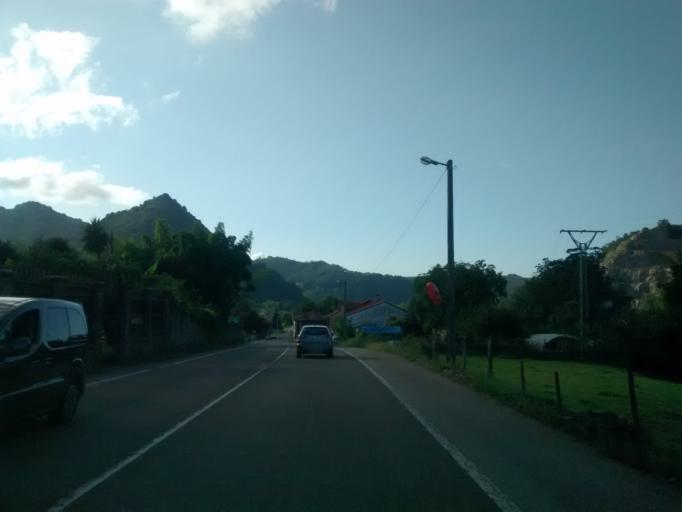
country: ES
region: Cantabria
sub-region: Provincia de Cantabria
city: Corvera
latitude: 43.2829
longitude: -3.9506
